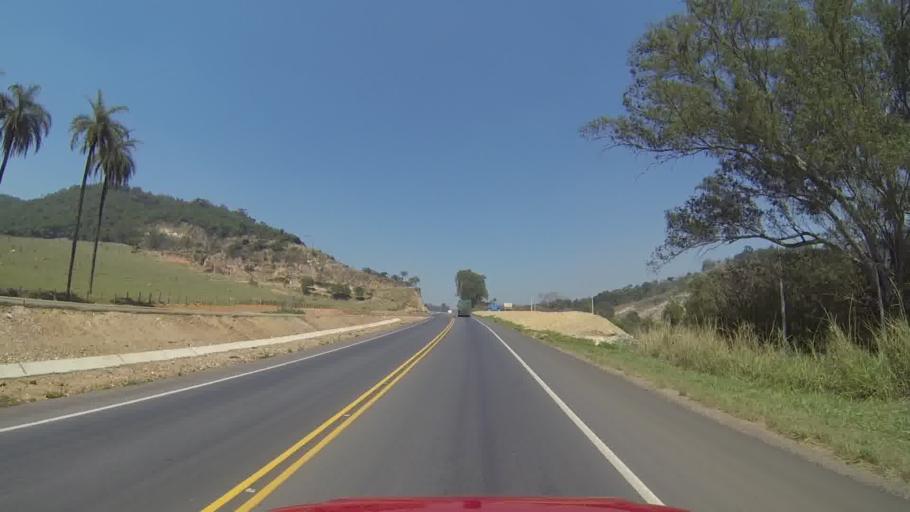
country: BR
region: Minas Gerais
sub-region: Mateus Leme
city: Mateus Leme
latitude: -20.0147
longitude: -44.4875
